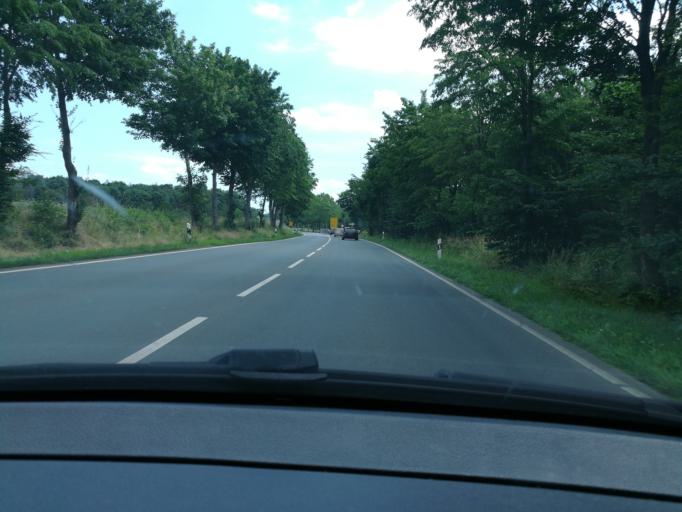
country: DE
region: North Rhine-Westphalia
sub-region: Regierungsbezirk Detmold
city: Petershagen
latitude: 52.3098
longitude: 8.9790
